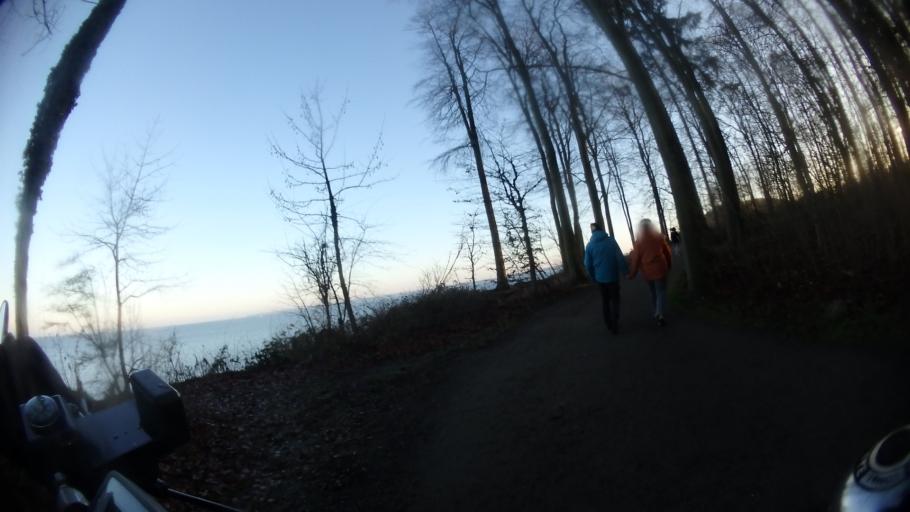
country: DE
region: Schleswig-Holstein
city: Travemuende
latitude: 53.9835
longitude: 10.8797
